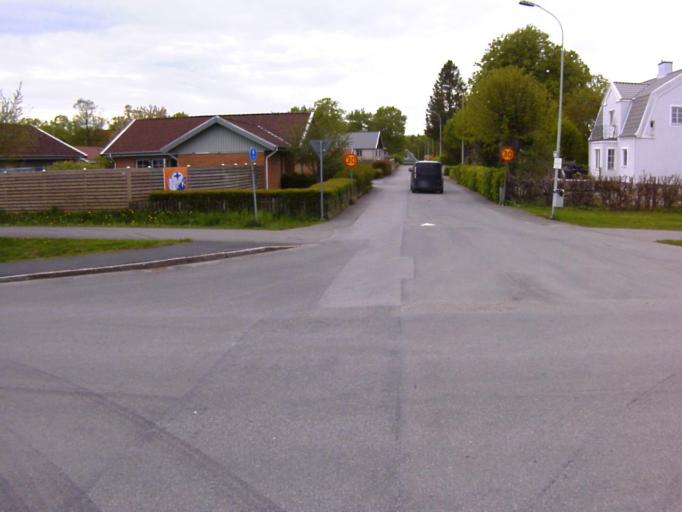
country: SE
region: Skane
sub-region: Kristianstads Kommun
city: Kristianstad
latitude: 56.0169
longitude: 14.1950
